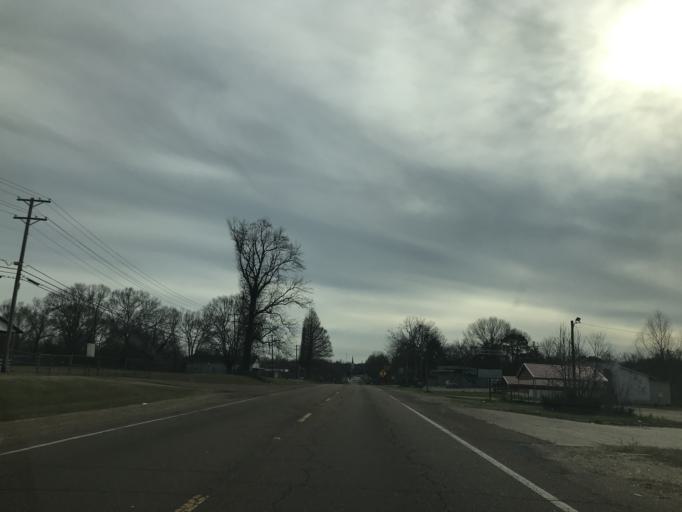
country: US
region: Mississippi
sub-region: Claiborne County
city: Port Gibson
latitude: 31.9714
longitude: -90.9781
